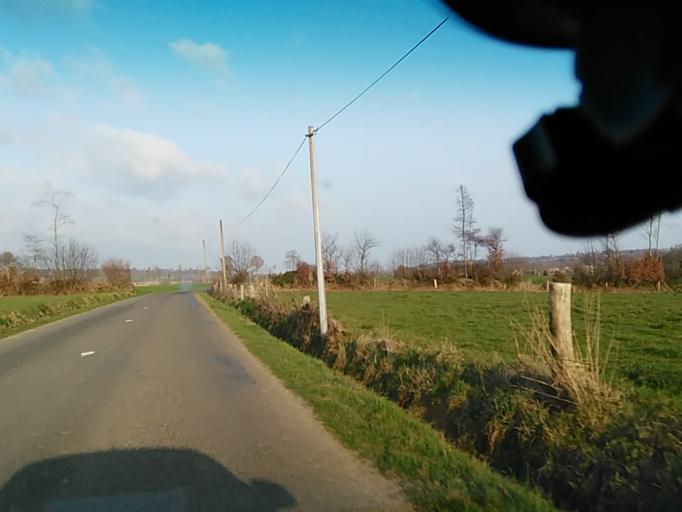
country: FR
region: Lower Normandy
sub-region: Departement de la Manche
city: Sourdeval
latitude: 48.7087
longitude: -0.8921
